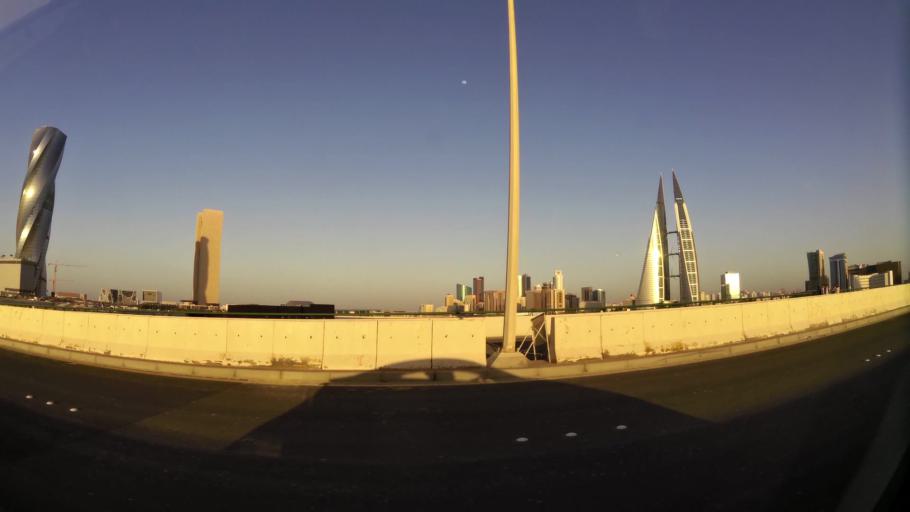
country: BH
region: Manama
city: Manama
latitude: 26.2421
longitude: 50.5745
